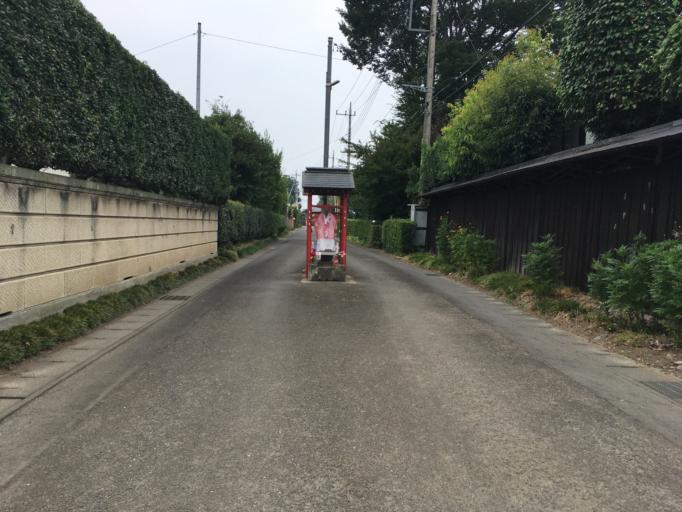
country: JP
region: Ibaraki
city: Shimodate
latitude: 36.3510
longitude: 139.9395
